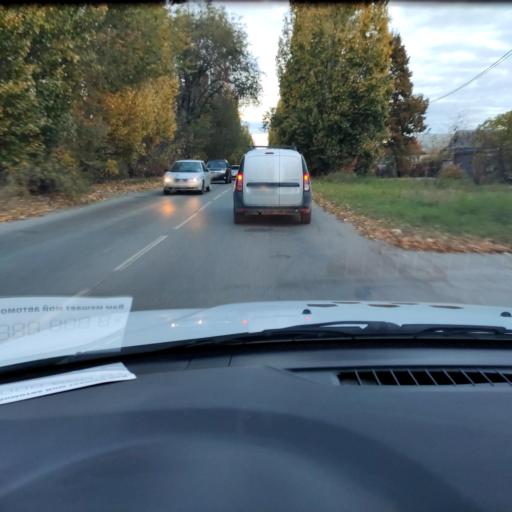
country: RU
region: Samara
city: Tol'yatti
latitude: 53.5320
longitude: 49.4184
